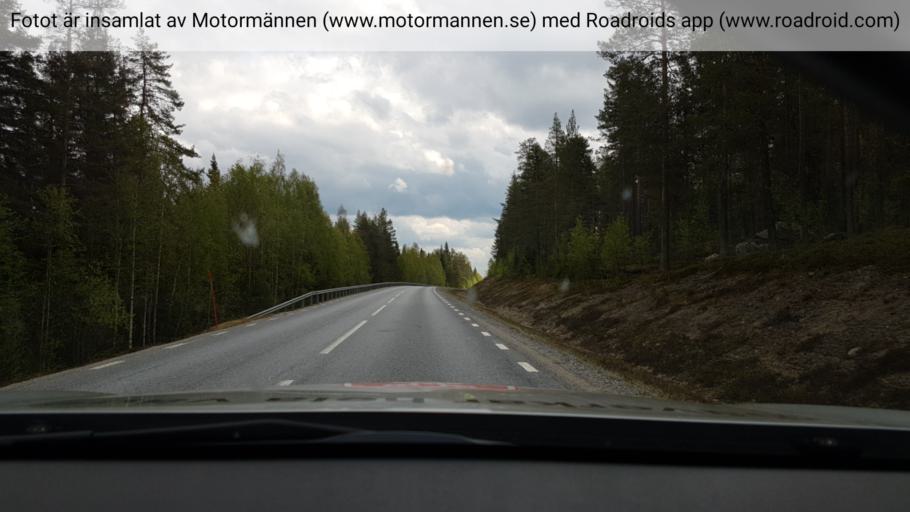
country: SE
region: Vaesterbotten
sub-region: Lycksele Kommun
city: Lycksele
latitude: 64.0316
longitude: 18.6266
